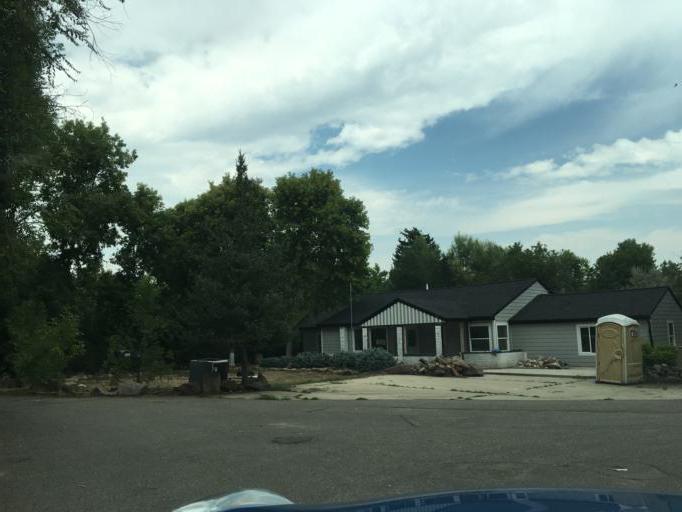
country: US
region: Colorado
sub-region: Jefferson County
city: Wheat Ridge
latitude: 39.7524
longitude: -105.0983
